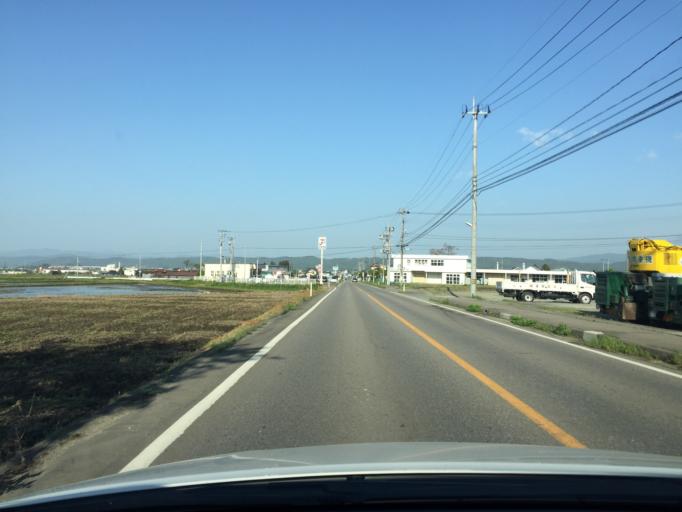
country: JP
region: Fukushima
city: Kitakata
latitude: 37.6569
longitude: 139.8973
